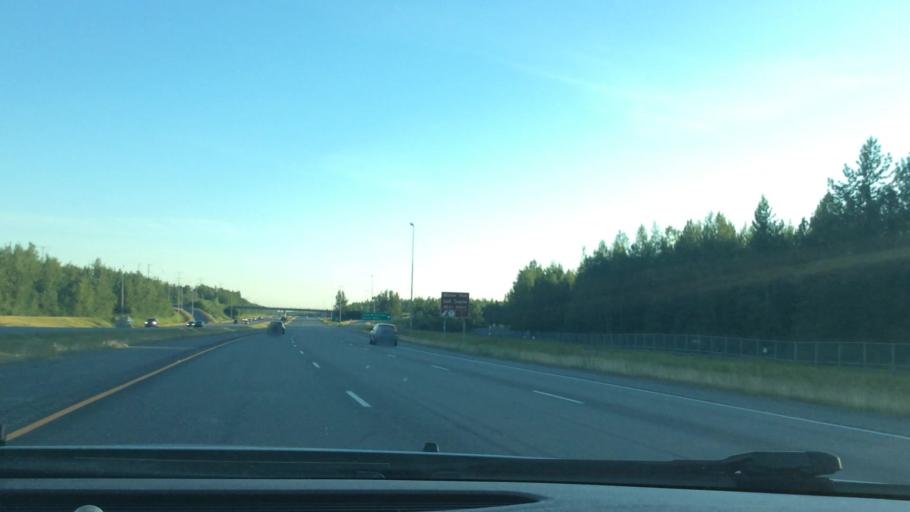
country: US
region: Alaska
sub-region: Anchorage Municipality
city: Elmendorf Air Force Base
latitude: 61.2569
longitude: -149.6511
